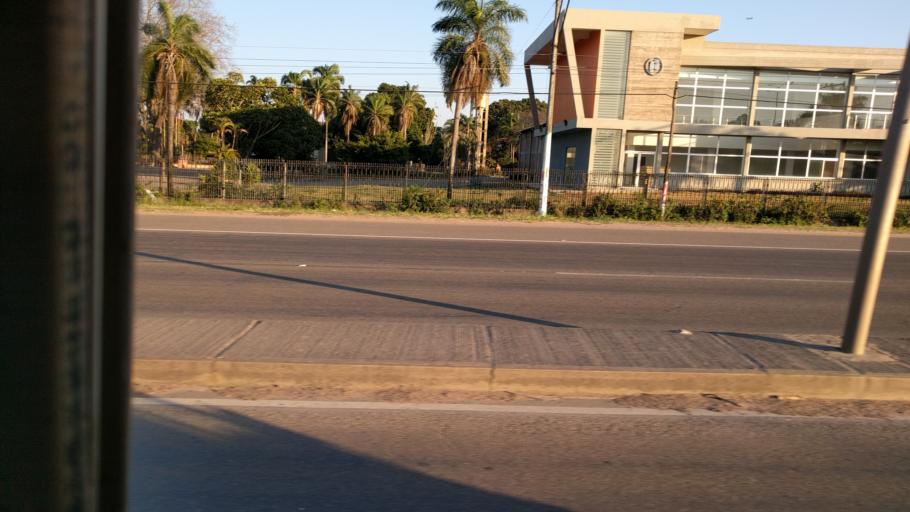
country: BO
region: Santa Cruz
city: Cotoca
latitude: -17.7639
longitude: -63.0322
